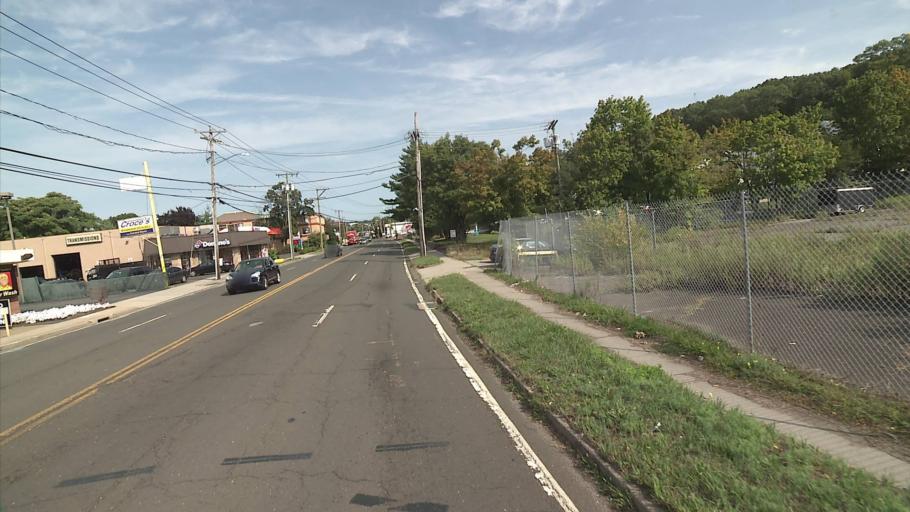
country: US
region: Connecticut
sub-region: Fairfield County
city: Norwalk
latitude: 41.1338
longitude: -73.4243
